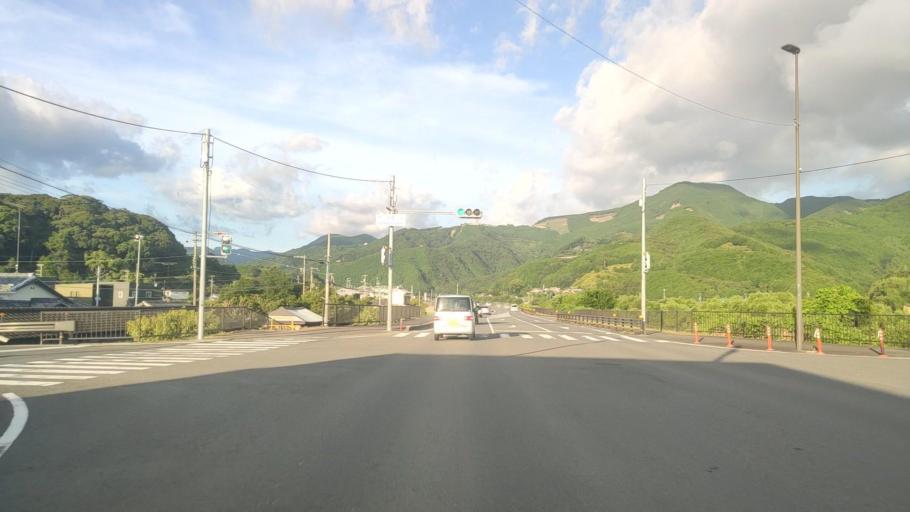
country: JP
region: Wakayama
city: Tanabe
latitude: 33.7157
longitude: 135.4669
